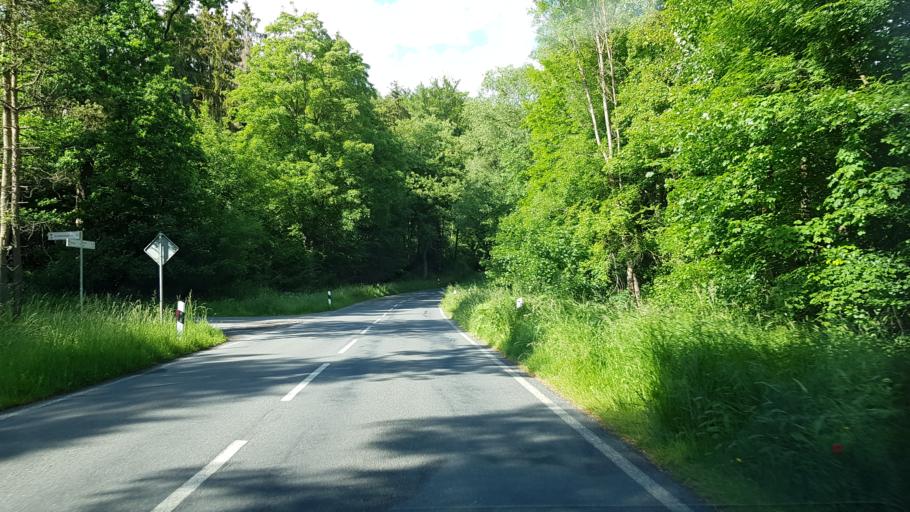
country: DE
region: Lower Saxony
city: Moringen
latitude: 51.7236
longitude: 9.8769
